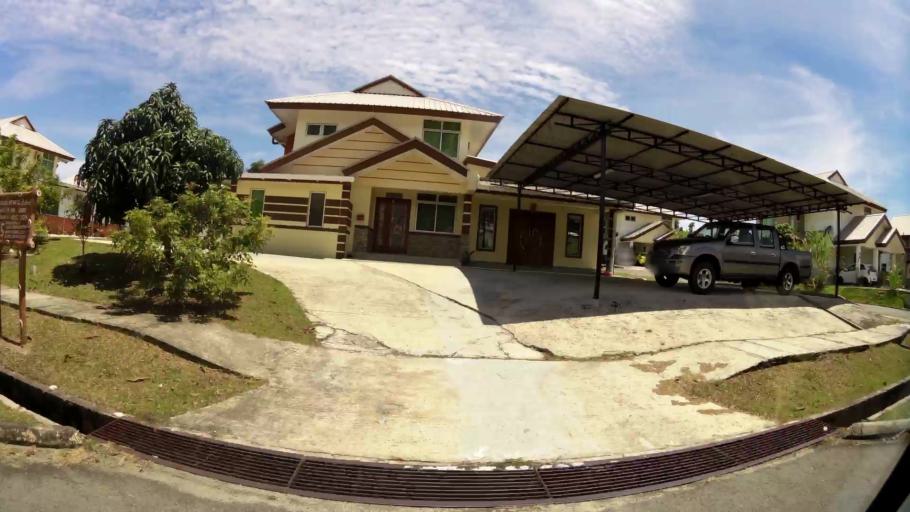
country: BN
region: Brunei and Muara
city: Bandar Seri Begawan
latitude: 4.9699
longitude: 114.9054
